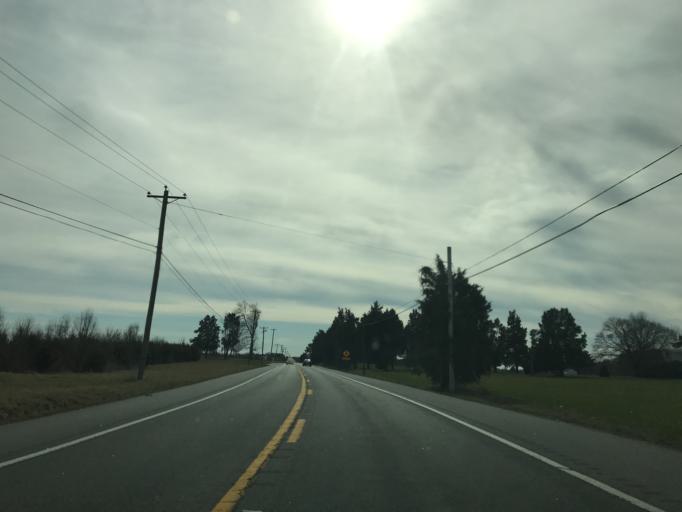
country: US
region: Maryland
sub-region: Queen Anne's County
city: Centreville
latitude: 39.0713
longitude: -76.0484
